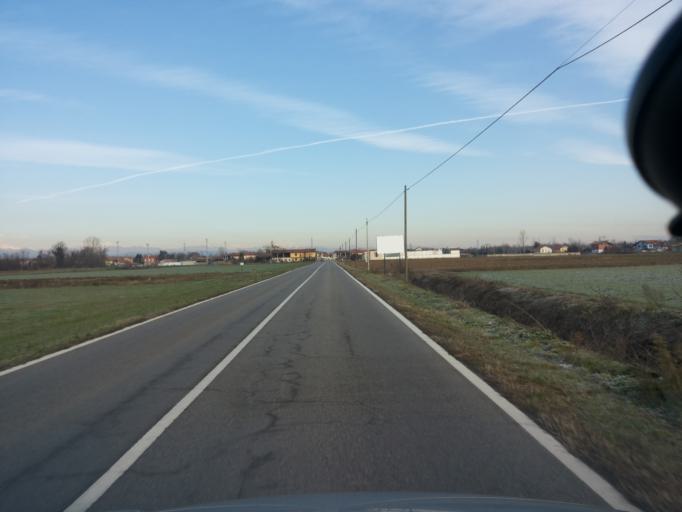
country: IT
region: Piedmont
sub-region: Provincia di Vercelli
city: Greggio
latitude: 45.4458
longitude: 8.3842
